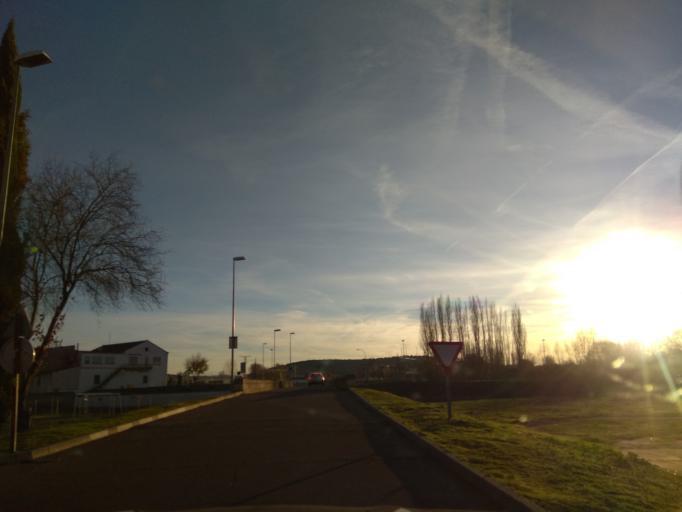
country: ES
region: Castille and Leon
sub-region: Provincia de Salamanca
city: Ciudad Rodrigo
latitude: 40.5933
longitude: -6.5384
